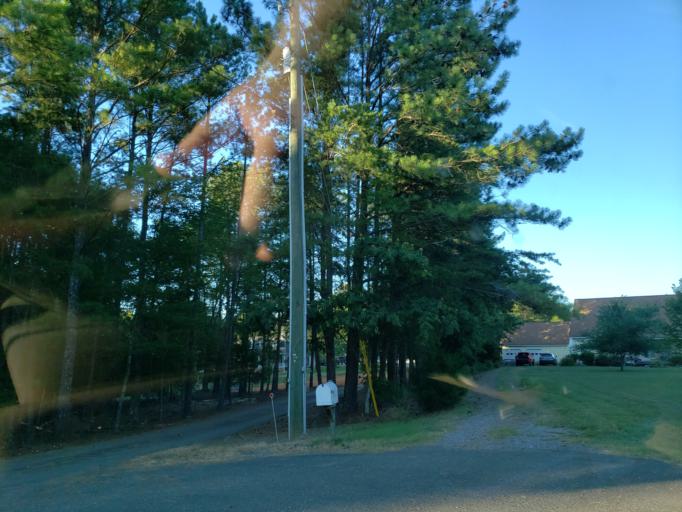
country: US
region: Georgia
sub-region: Bartow County
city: Euharlee
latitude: 34.0933
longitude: -84.9665
